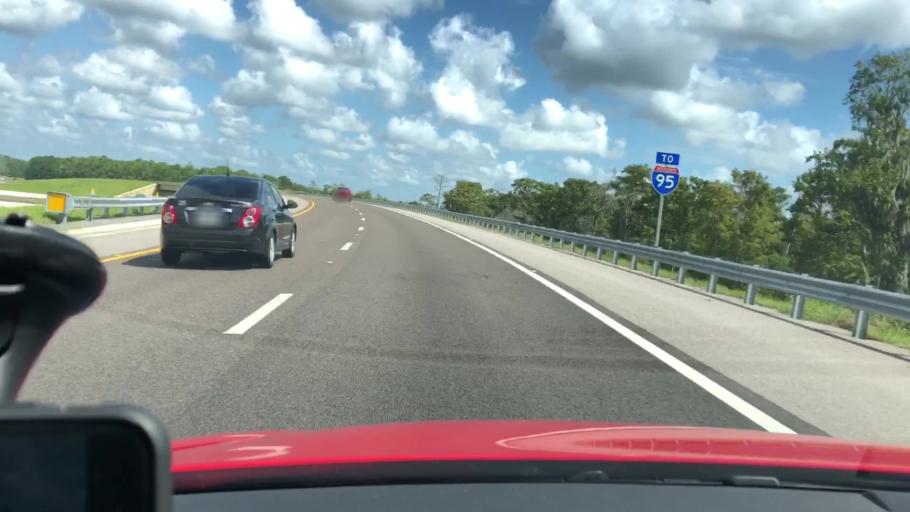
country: US
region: Florida
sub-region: Volusia County
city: Samsula-Spruce Creek
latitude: 29.1345
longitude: -81.1193
